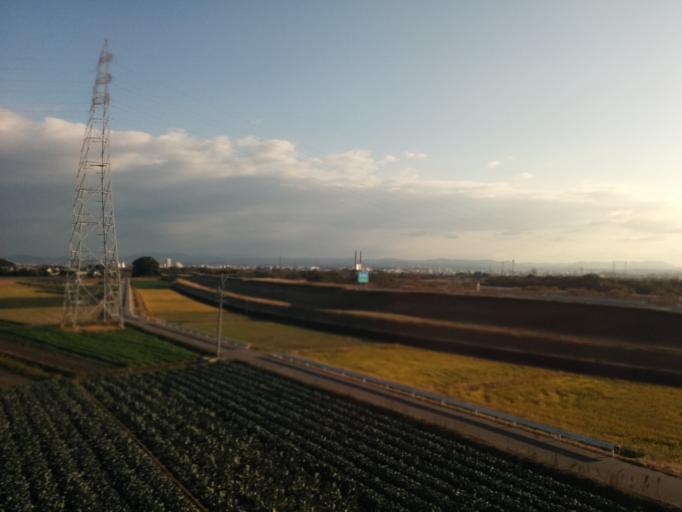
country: JP
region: Aichi
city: Anjo
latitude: 34.9191
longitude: 137.1063
